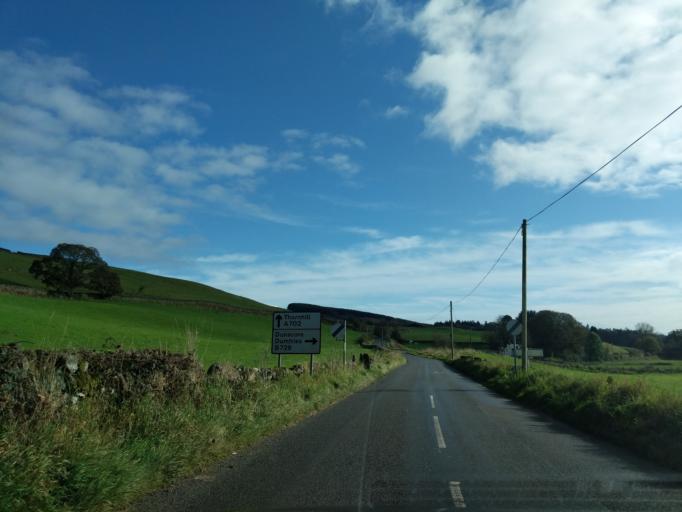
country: GB
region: Scotland
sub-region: Dumfries and Galloway
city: Thornhill
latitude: 55.1929
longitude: -3.8687
